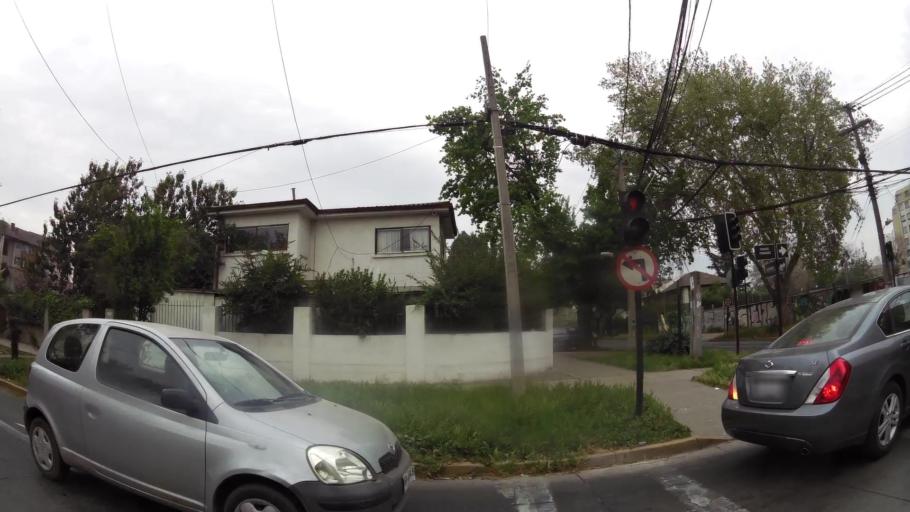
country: CL
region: Santiago Metropolitan
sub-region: Provincia de Santiago
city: Villa Presidente Frei, Nunoa, Santiago, Chile
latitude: -33.4690
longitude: -70.6005
